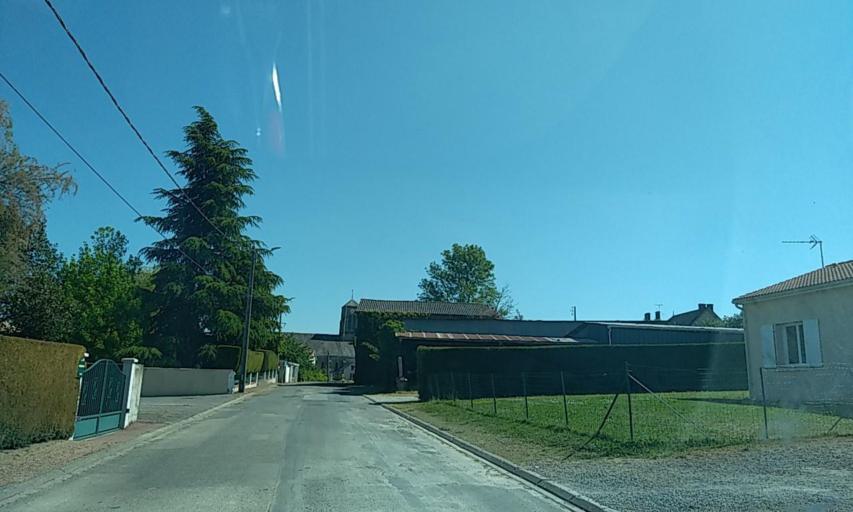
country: FR
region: Poitou-Charentes
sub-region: Departement des Deux-Sevres
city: Boisme
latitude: 46.7758
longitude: -0.4363
